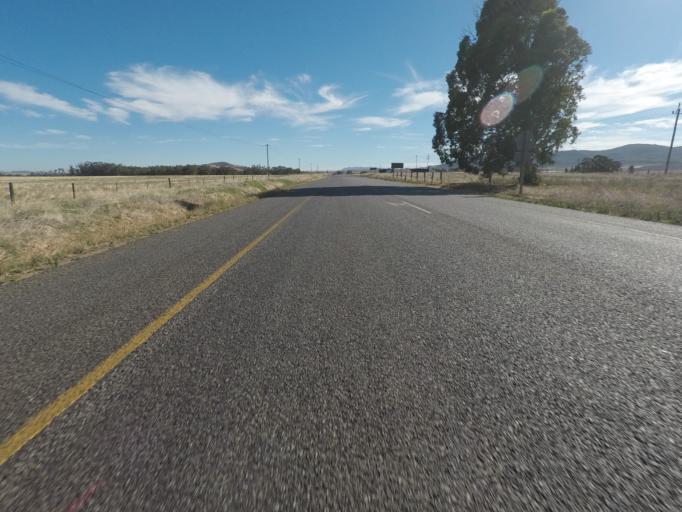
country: ZA
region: Western Cape
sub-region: West Coast District Municipality
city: Malmesbury
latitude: -33.6230
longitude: 18.7251
